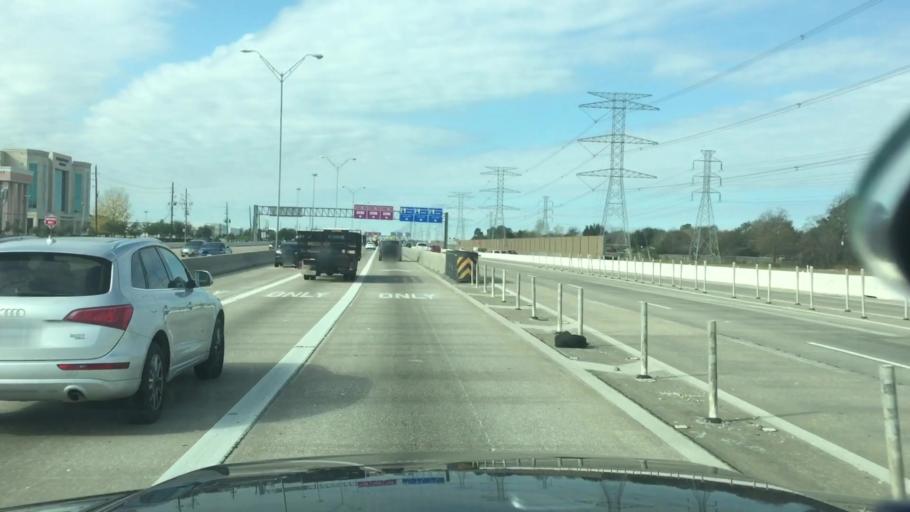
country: US
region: Texas
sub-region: Harris County
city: Hudson
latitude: 29.9378
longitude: -95.4650
